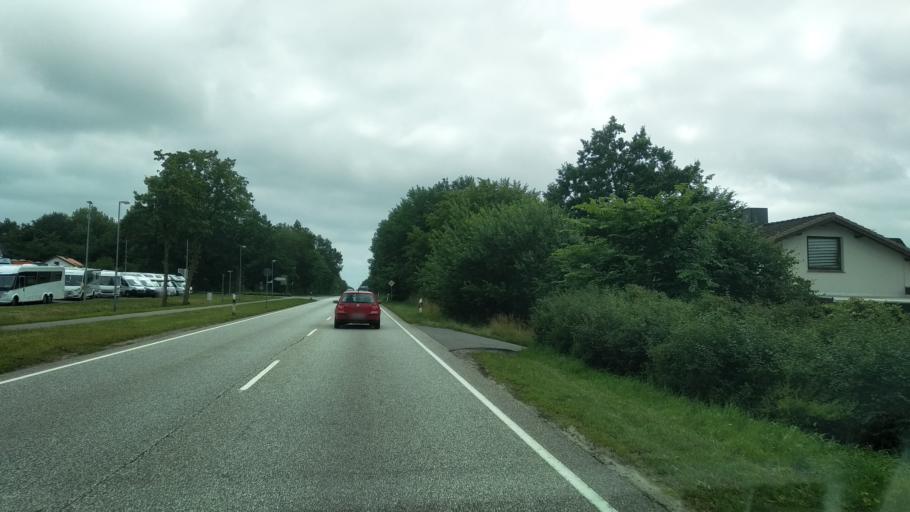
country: DE
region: Schleswig-Holstein
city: Oeversee
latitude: 54.7012
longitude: 9.4360
